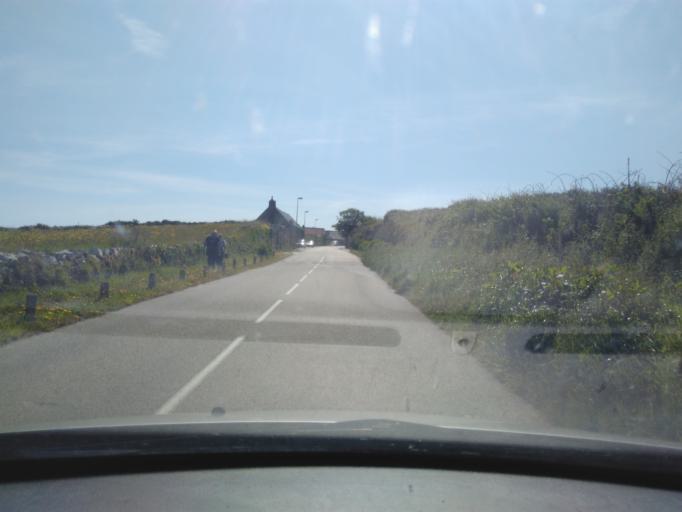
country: FR
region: Lower Normandy
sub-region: Departement de la Manche
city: Beaumont-Hague
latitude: 49.7141
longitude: -1.9331
